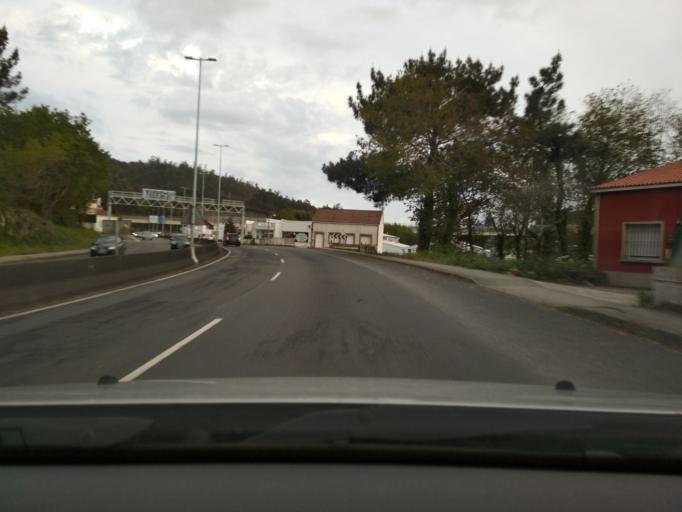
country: ES
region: Galicia
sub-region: Provincia da Coruna
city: Santiago de Compostela
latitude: 42.8589
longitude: -8.5720
